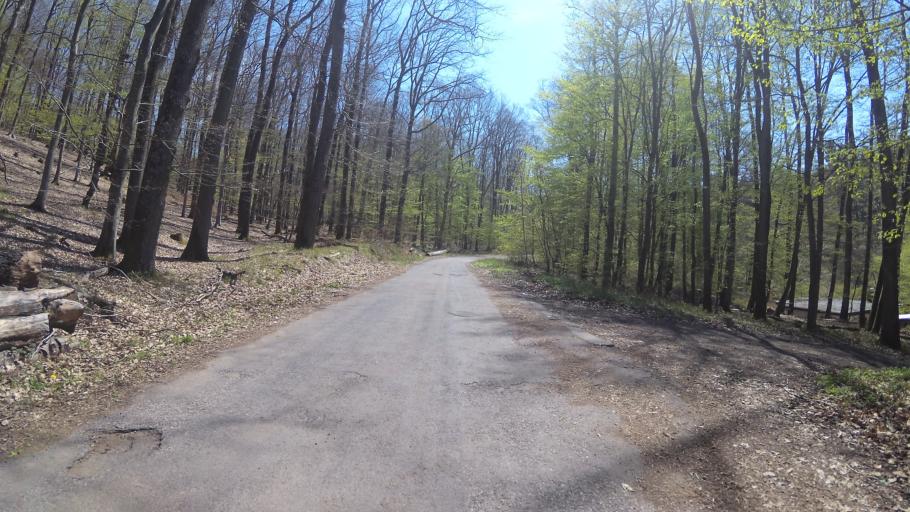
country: DE
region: Rheinland-Pfalz
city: Breitenbach
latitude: 49.4141
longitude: 7.2723
